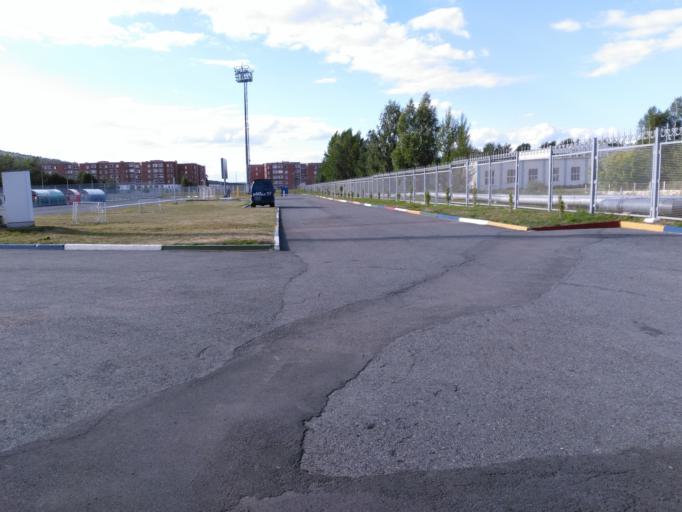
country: RU
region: Bashkortostan
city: Uchaly
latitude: 54.3201
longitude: 59.3713
